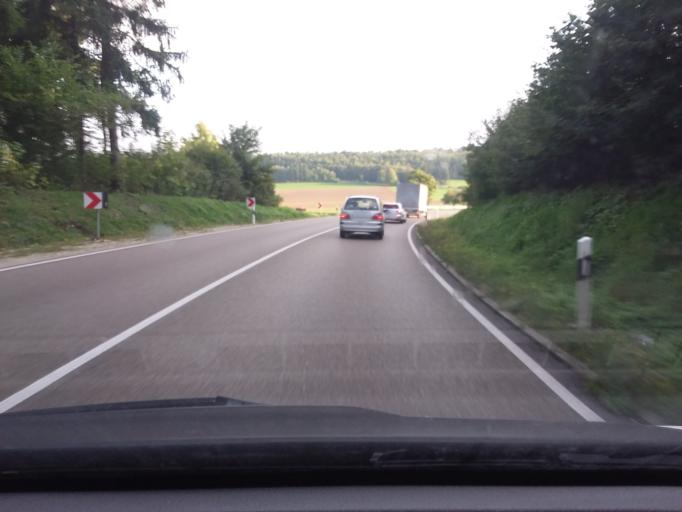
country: DE
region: Baden-Wuerttemberg
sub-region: Tuebingen Region
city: Lonsee
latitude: 48.5084
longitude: 9.9198
